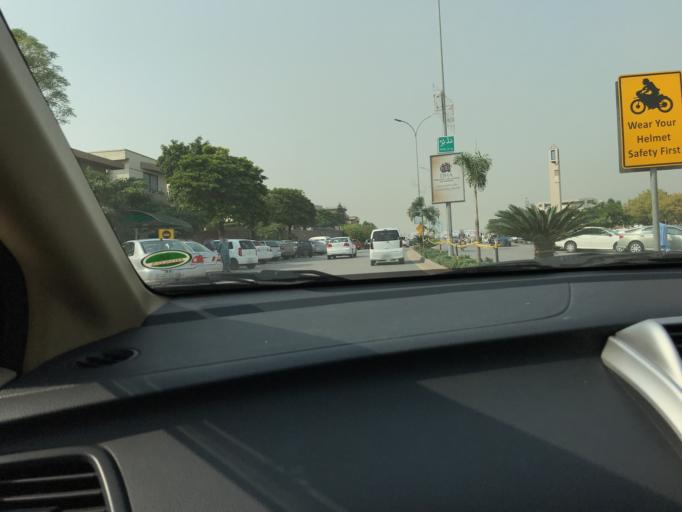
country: PK
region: Punjab
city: Rawalpindi
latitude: 33.5394
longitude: 73.0987
